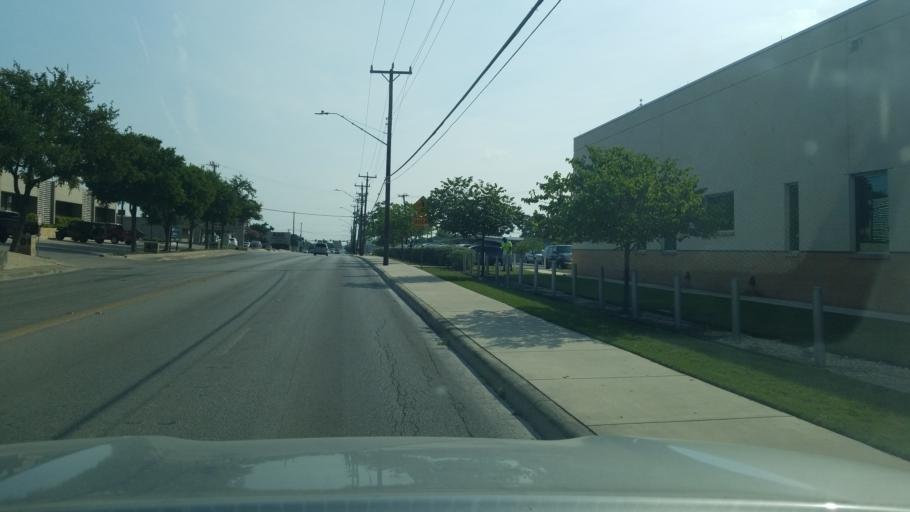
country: US
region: Texas
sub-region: Bexar County
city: Castle Hills
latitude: 29.5263
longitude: -98.4952
